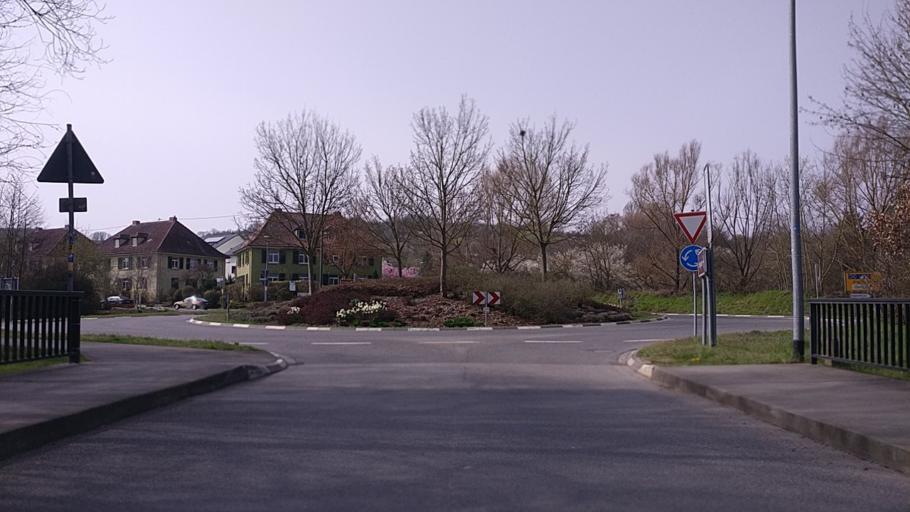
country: DE
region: Rheinland-Pfalz
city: Ingelheim am Rhein
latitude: 49.9617
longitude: 8.0546
